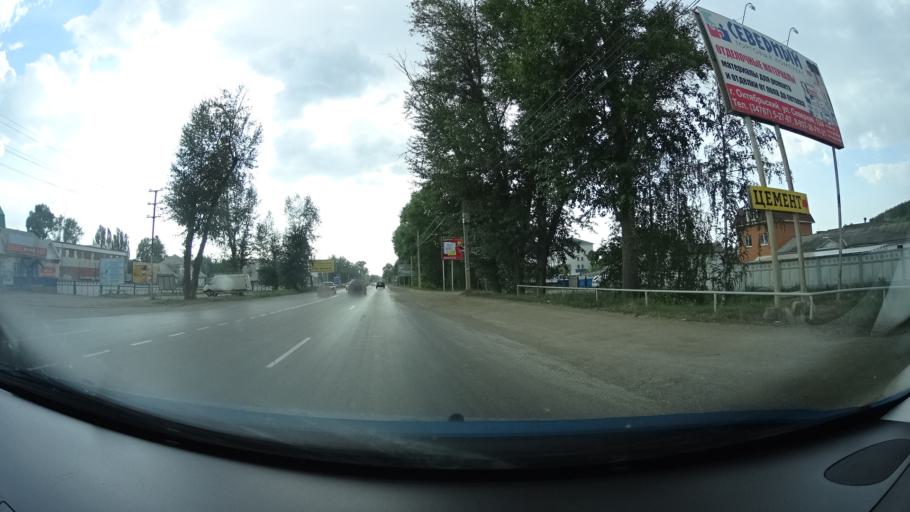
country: RU
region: Bashkortostan
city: Oktyabr'skiy
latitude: 54.4919
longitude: 53.4646
